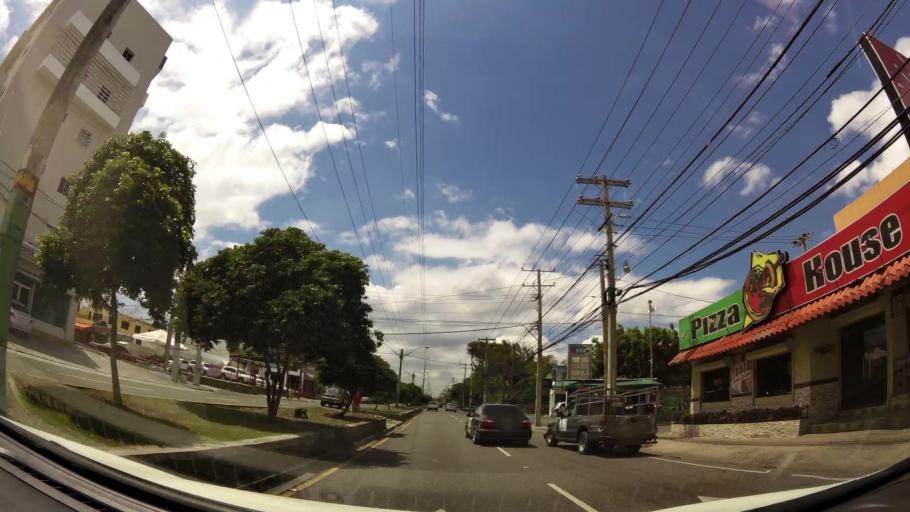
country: DO
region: Nacional
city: Bella Vista
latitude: 18.4371
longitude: -69.9554
